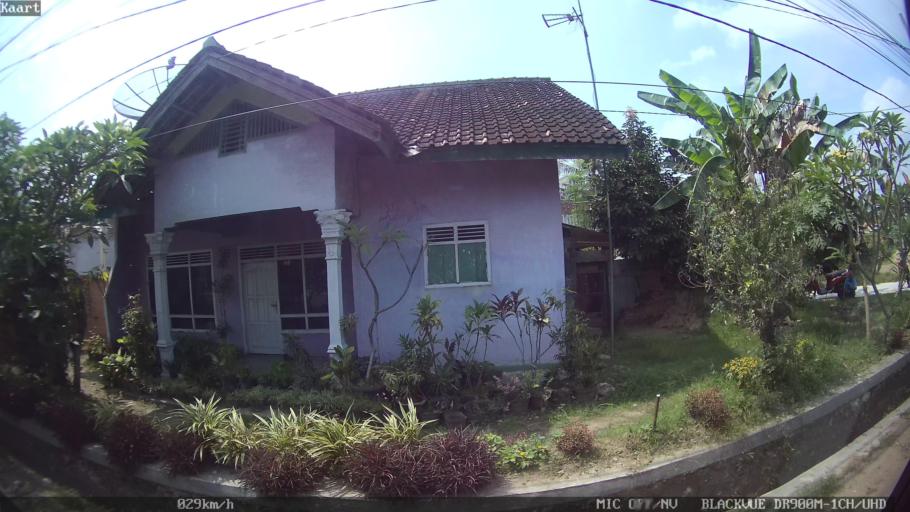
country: ID
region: Lampung
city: Pringsewu
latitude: -5.3661
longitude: 104.9712
